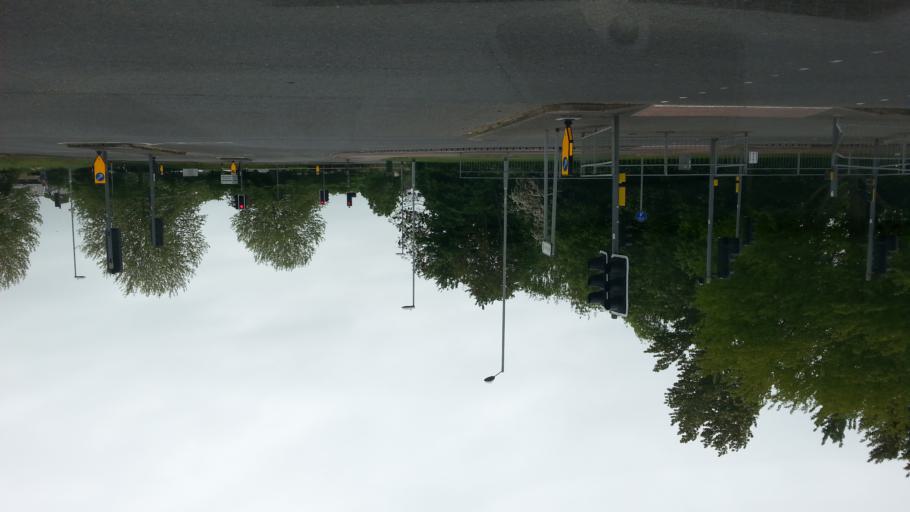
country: GB
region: England
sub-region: Cambridgeshire
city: Histon
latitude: 52.2318
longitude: 0.1187
